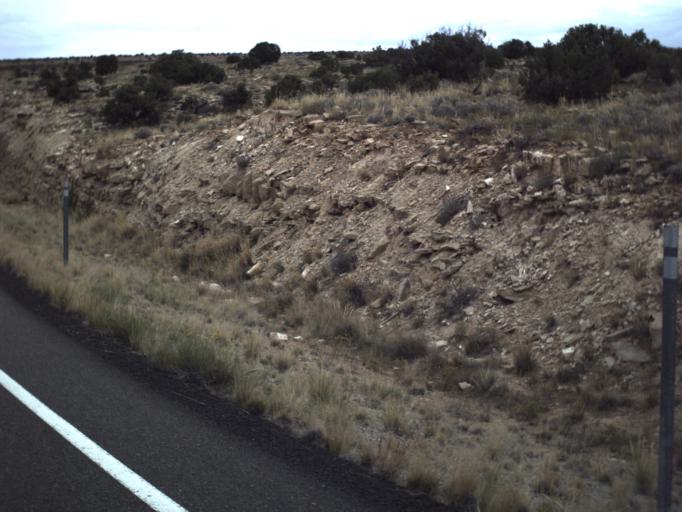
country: US
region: Utah
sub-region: Emery County
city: Castle Dale
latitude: 38.9340
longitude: -110.4728
